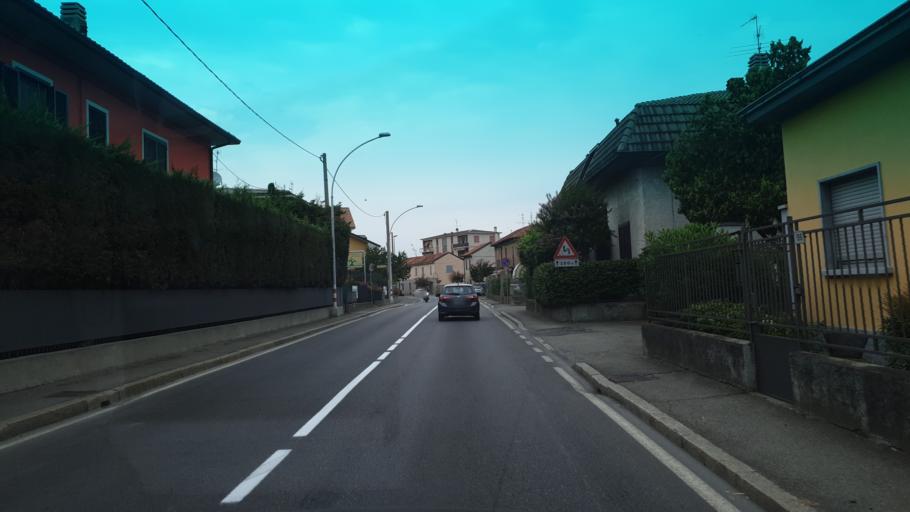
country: IT
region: Lombardy
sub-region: Provincia di Bergamo
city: Fara Gera d'Adda
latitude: 45.5521
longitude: 9.5350
